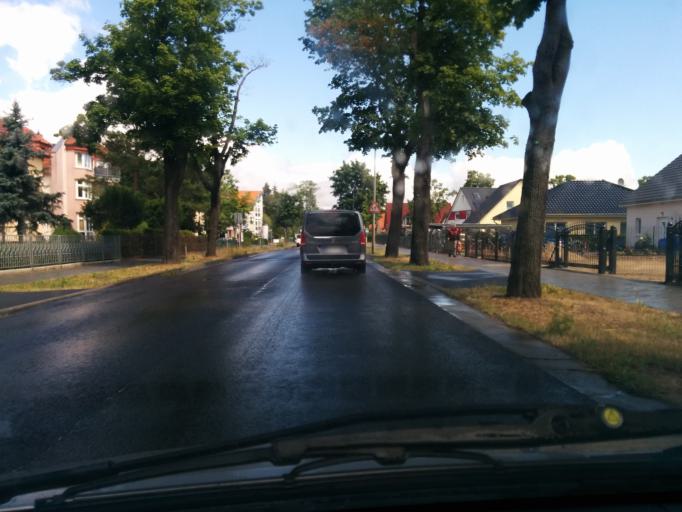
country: DE
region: Brandenburg
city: Falkensee
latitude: 52.5697
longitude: 13.1045
